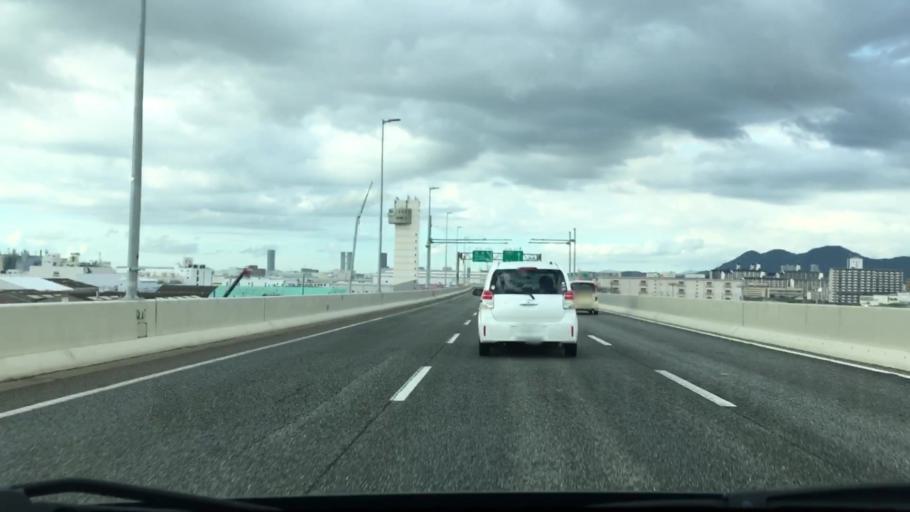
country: JP
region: Fukuoka
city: Fukuoka-shi
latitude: 33.6187
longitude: 130.4124
